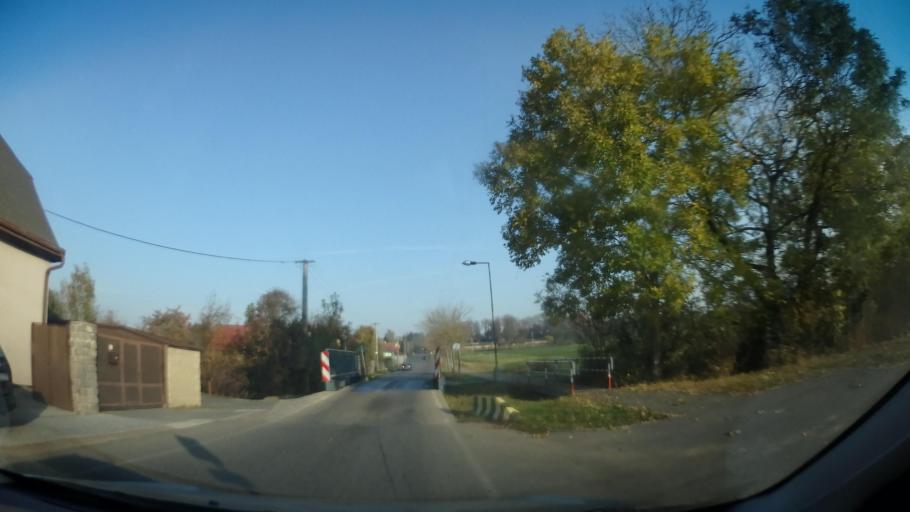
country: CZ
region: Central Bohemia
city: Jirny
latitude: 50.1110
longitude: 14.7028
